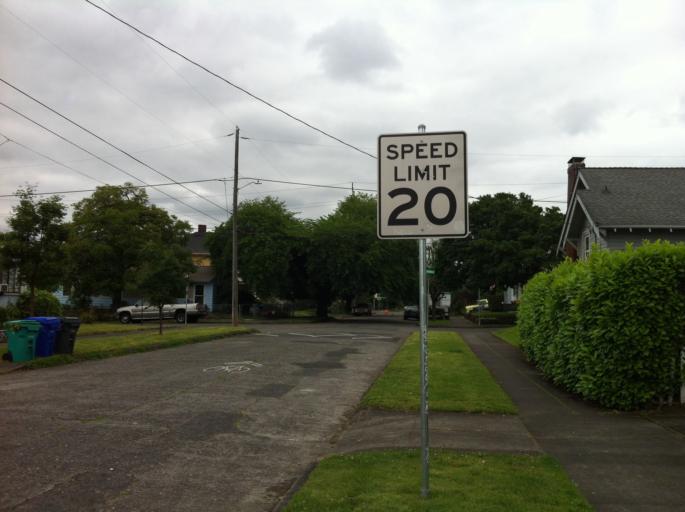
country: US
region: Oregon
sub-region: Multnomah County
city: Portland
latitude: 45.5733
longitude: -122.6683
